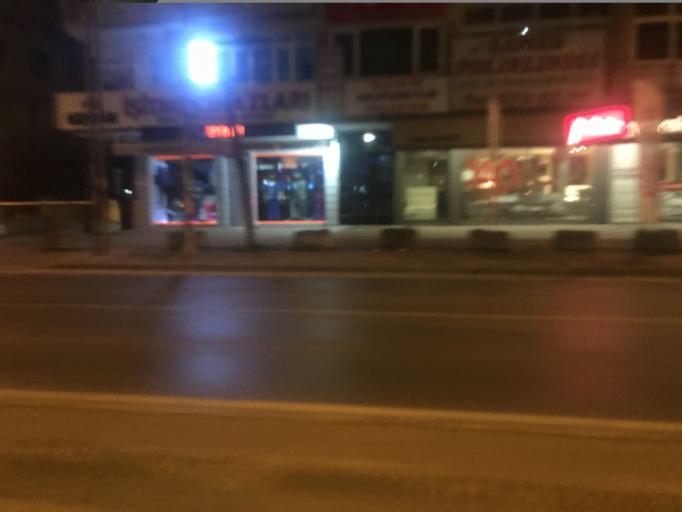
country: TR
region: Istanbul
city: Bahcelievler
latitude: 40.9858
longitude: 28.8722
